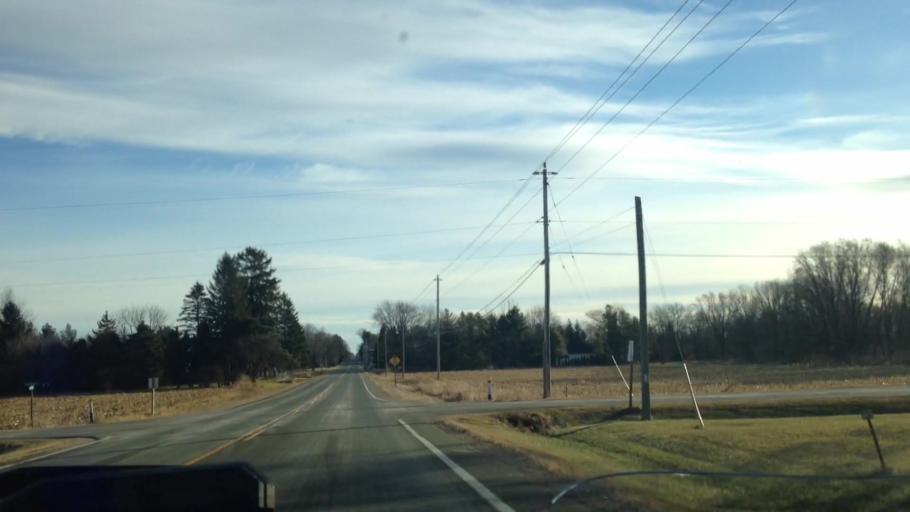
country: US
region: Wisconsin
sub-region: Washington County
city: Germantown
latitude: 43.2941
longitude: -88.1032
